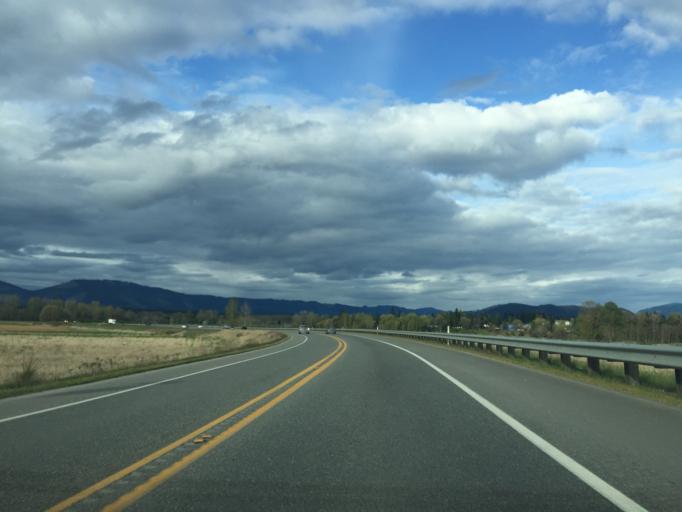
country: US
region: Washington
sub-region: Snohomish County
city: Arlington
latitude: 48.1894
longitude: -122.1416
